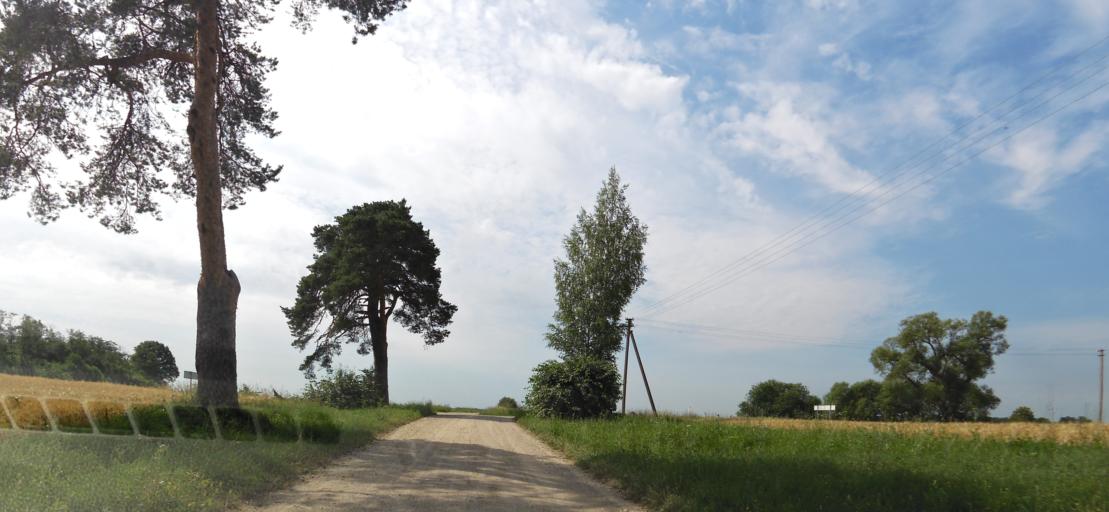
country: LT
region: Panevezys
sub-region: Birzai
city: Birzai
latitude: 56.2123
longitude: 24.6807
